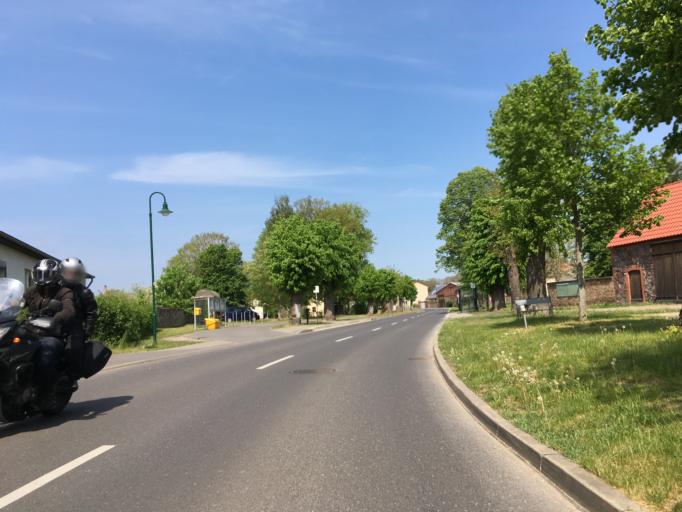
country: DE
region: Brandenburg
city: Melchow
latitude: 52.7093
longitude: 13.7184
